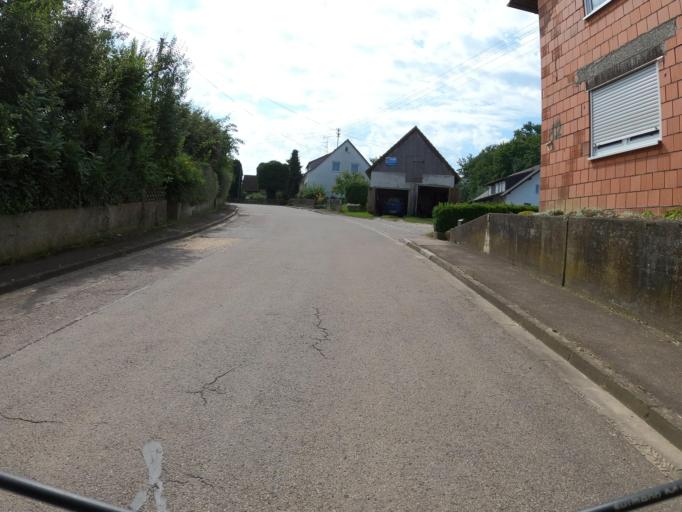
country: DE
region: Bavaria
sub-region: Swabia
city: Rieden an der Kotz
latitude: 48.3813
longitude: 10.2114
